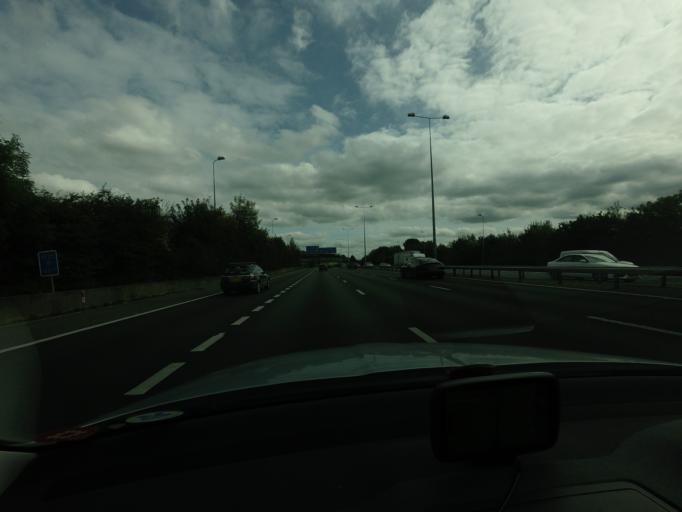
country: GB
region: England
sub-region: Surrey
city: Godstone
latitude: 51.2583
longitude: -0.0741
